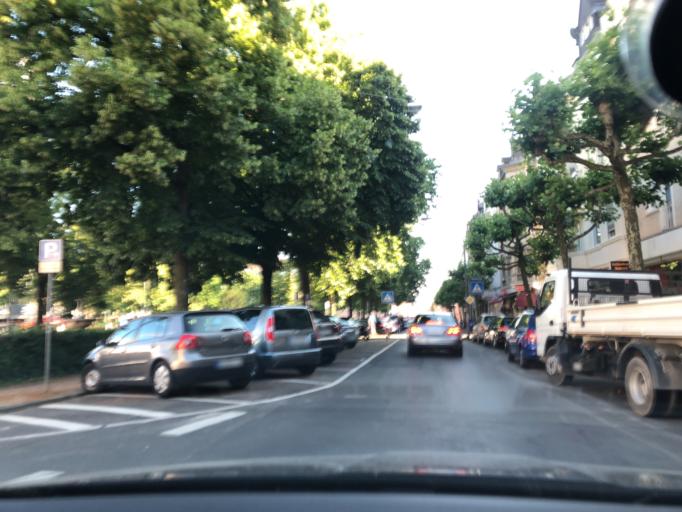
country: DE
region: Hesse
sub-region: Regierungsbezirk Darmstadt
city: Wiesbaden
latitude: 50.0444
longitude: 8.2409
